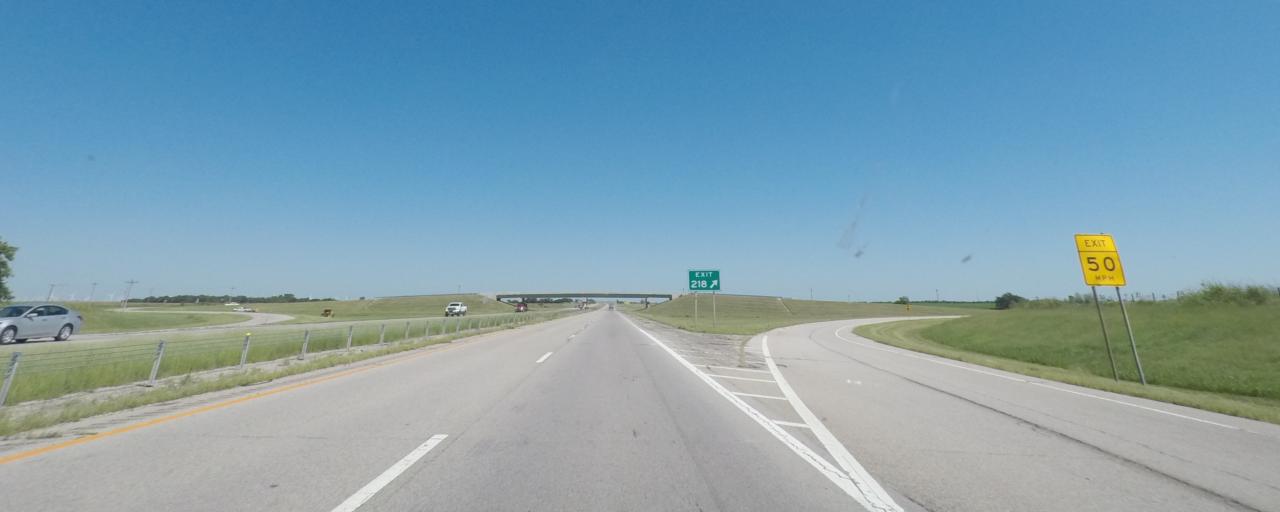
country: US
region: Oklahoma
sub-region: Kay County
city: Tonkawa
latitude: 36.7506
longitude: -97.3458
